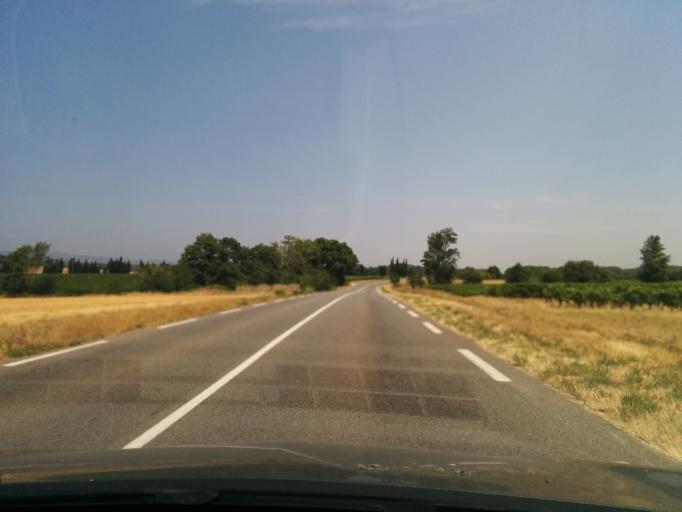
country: FR
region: Languedoc-Roussillon
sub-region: Departement de l'Aude
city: Alzonne
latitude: 43.2614
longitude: 2.2095
